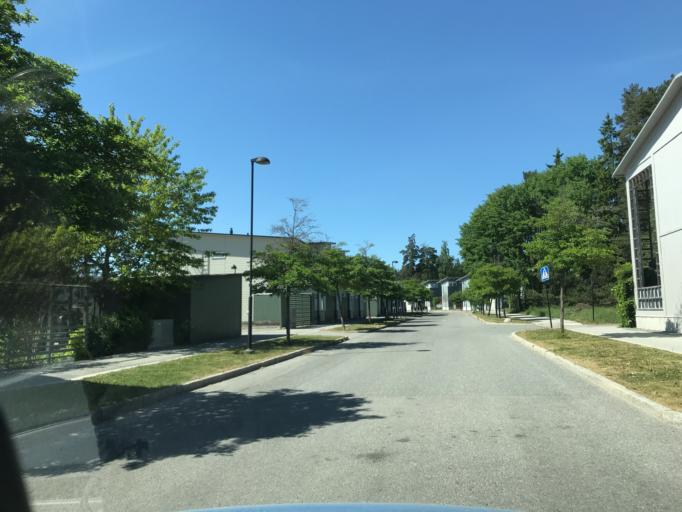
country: SE
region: Stockholm
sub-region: Solna Kommun
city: Rasunda
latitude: 59.4016
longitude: 17.9884
